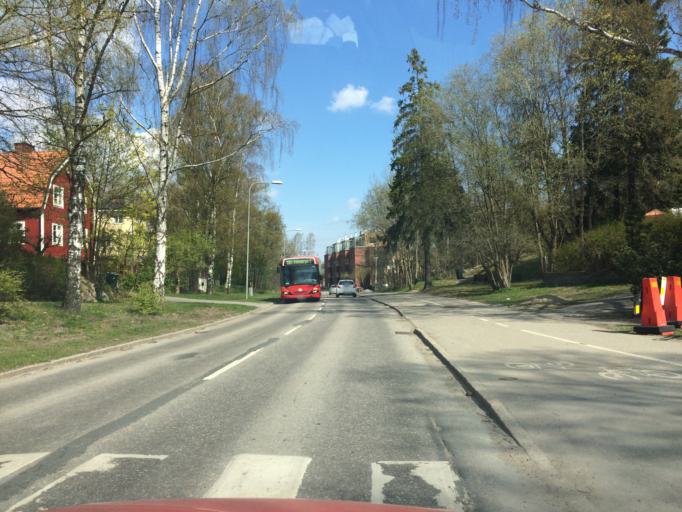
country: SE
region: Stockholm
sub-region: Huddinge Kommun
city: Segeltorp
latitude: 59.2946
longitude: 17.9546
